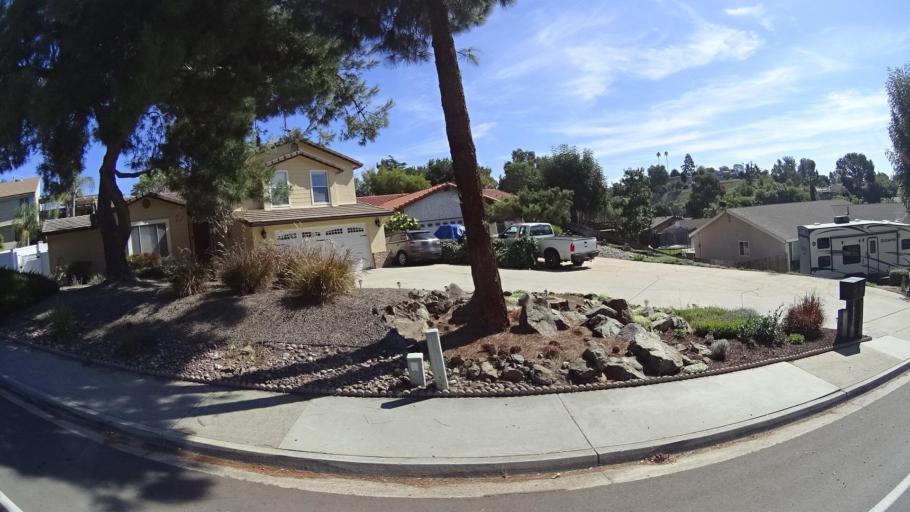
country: US
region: California
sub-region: San Diego County
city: Casa de Oro-Mount Helix
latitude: 32.7543
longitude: -116.9733
